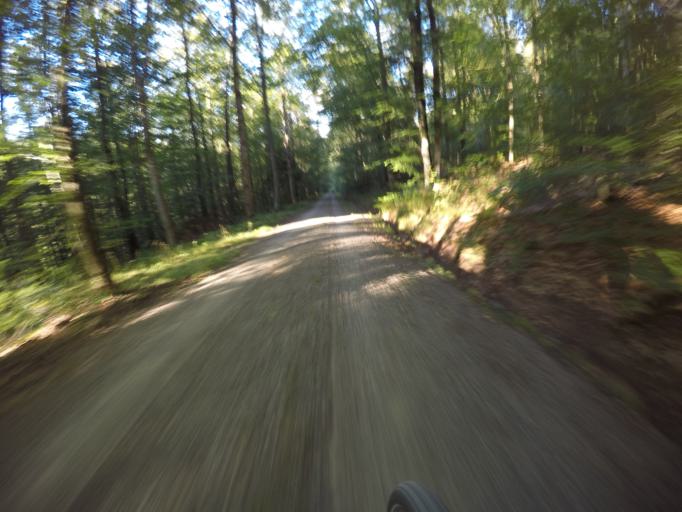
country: DE
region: Baden-Wuerttemberg
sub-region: Regierungsbezirk Stuttgart
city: Waldenbuch
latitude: 48.6401
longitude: 9.1096
